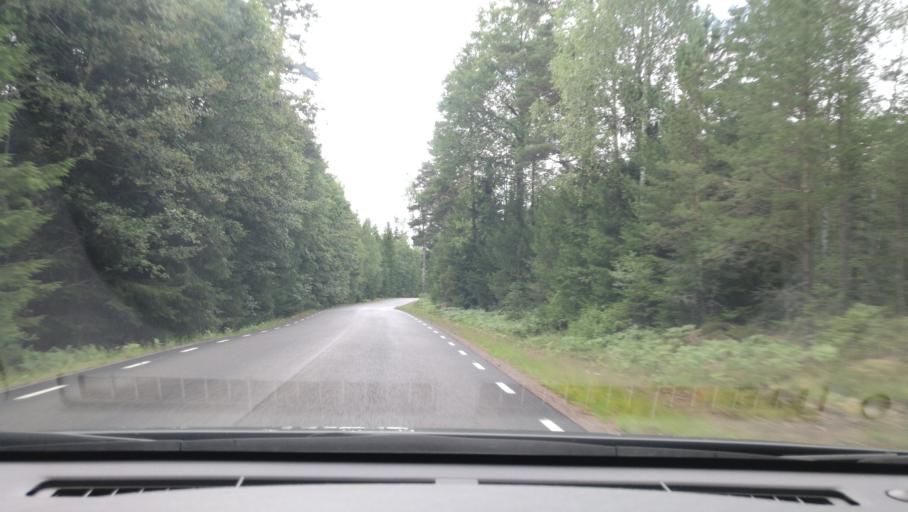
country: SE
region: OEstergoetland
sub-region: Norrkopings Kommun
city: Svartinge
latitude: 58.8166
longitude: 16.0748
